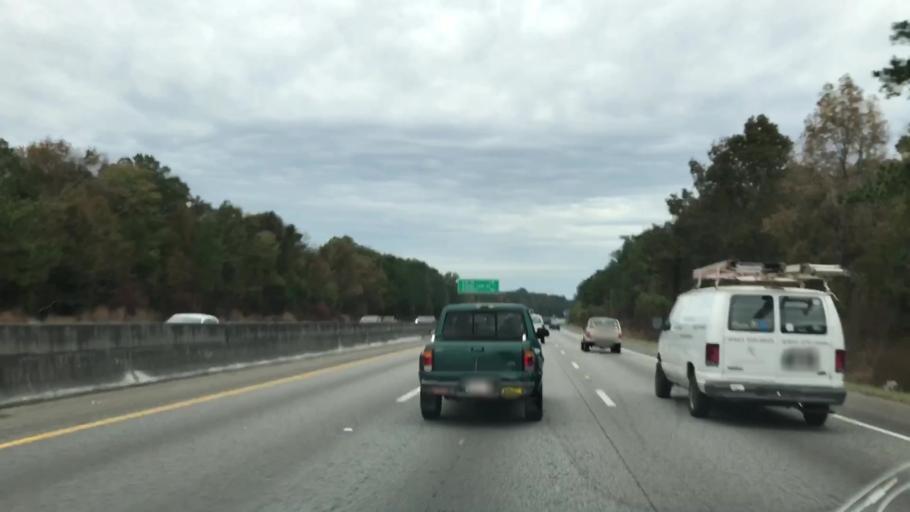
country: US
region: South Carolina
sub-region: Berkeley County
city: Goose Creek
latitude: 32.9577
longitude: -80.0680
